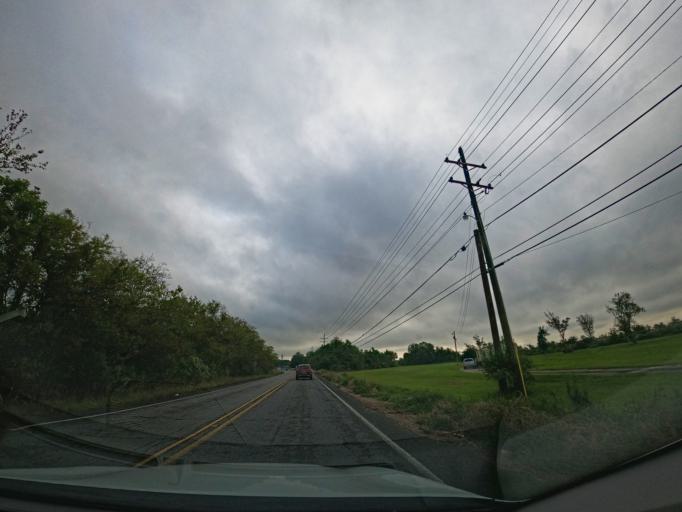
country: US
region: Louisiana
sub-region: Terrebonne Parish
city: Presquille
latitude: 29.4974
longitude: -90.6843
